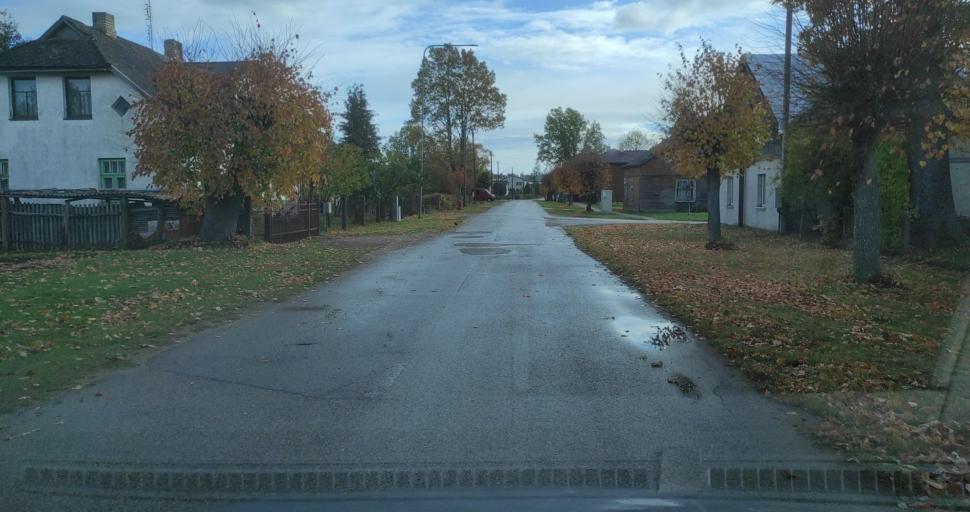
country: LV
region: Skrunda
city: Skrunda
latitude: 56.6724
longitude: 22.0122
